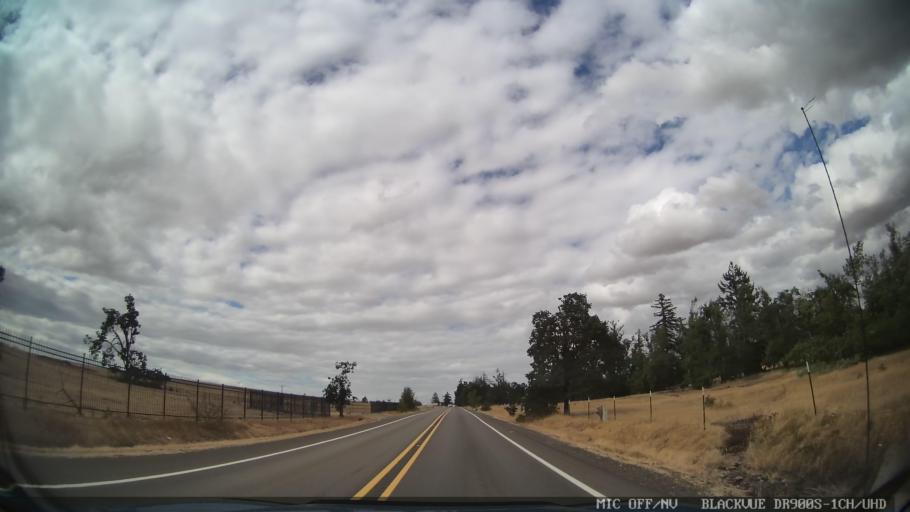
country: US
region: Oregon
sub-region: Marion County
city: Sublimity
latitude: 44.8530
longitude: -122.7933
